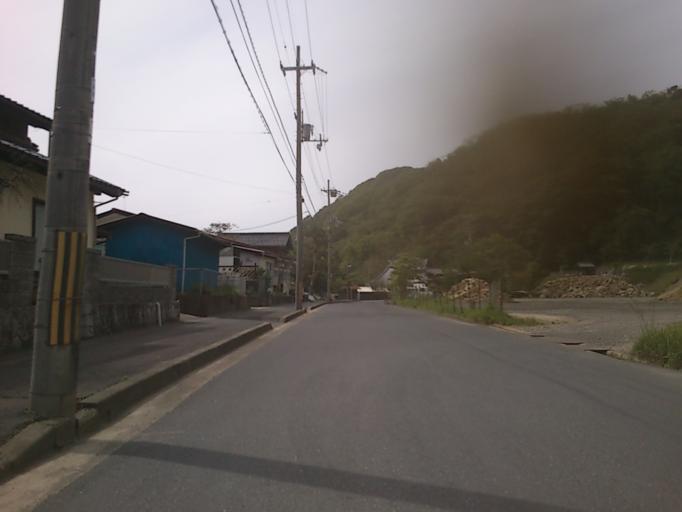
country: JP
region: Hyogo
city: Toyooka
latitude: 35.6679
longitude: 134.9704
